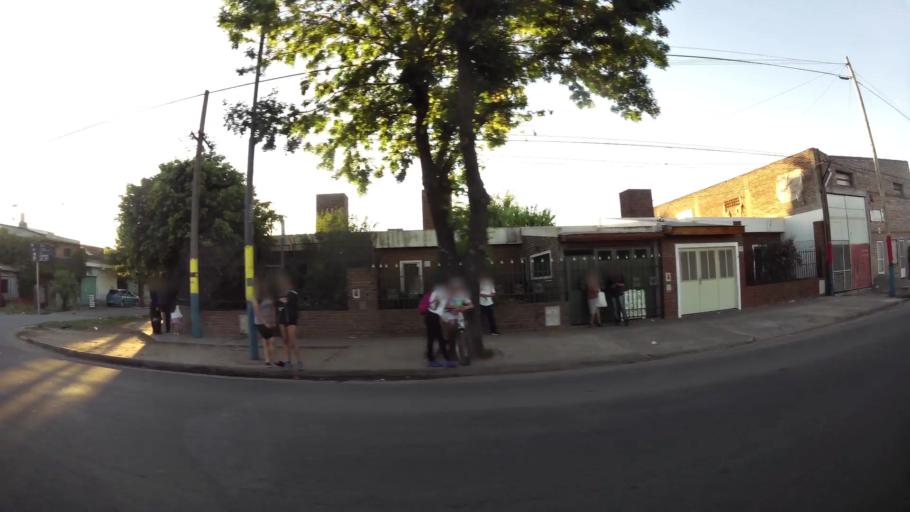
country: AR
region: Santa Fe
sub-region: Departamento de Rosario
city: Rosario
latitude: -32.9682
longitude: -60.6865
